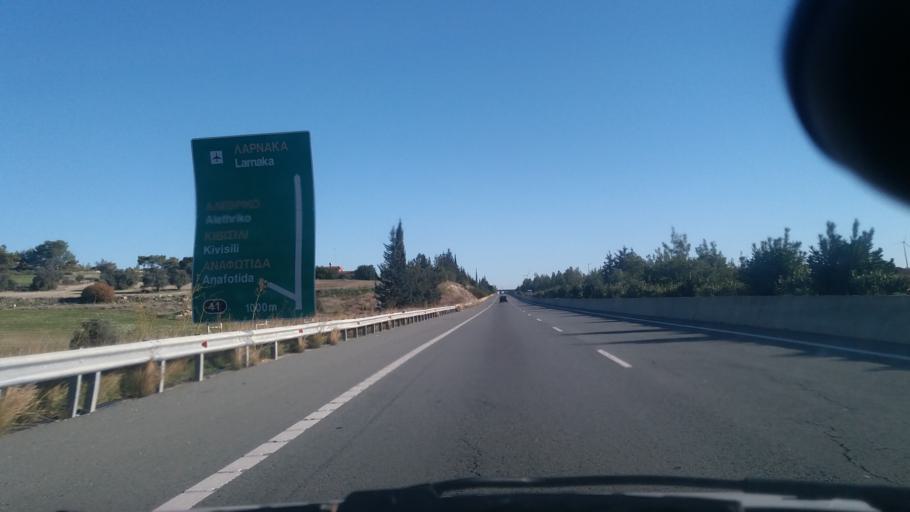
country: CY
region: Larnaka
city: Tersefanou
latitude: 34.8651
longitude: 33.4833
